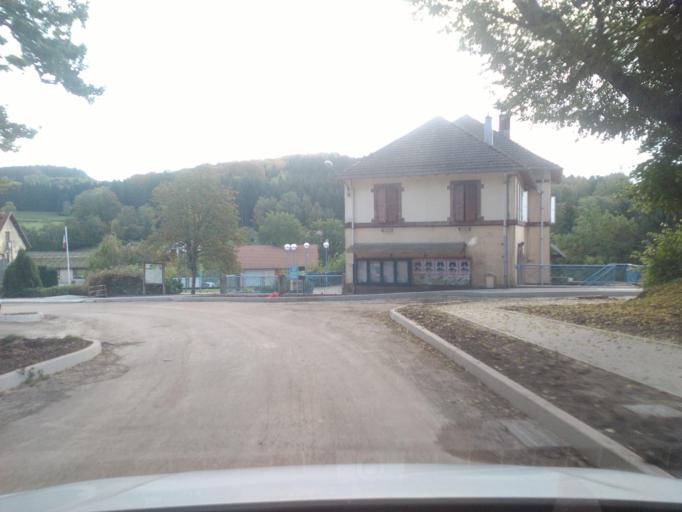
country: FR
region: Lorraine
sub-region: Departement des Vosges
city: Senones
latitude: 48.3433
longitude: 7.0130
